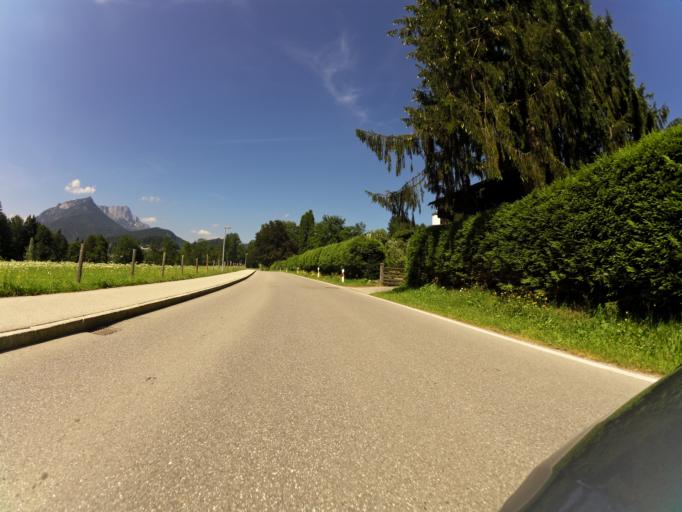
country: DE
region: Bavaria
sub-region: Upper Bavaria
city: Schoenau am Koenigssee
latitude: 47.6184
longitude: 12.9838
